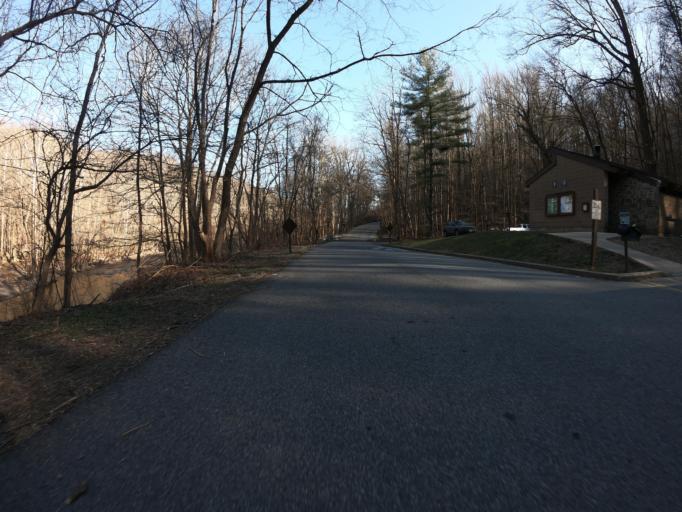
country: US
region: Maryland
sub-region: Howard County
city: Ilchester
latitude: 39.2408
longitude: -76.7498
